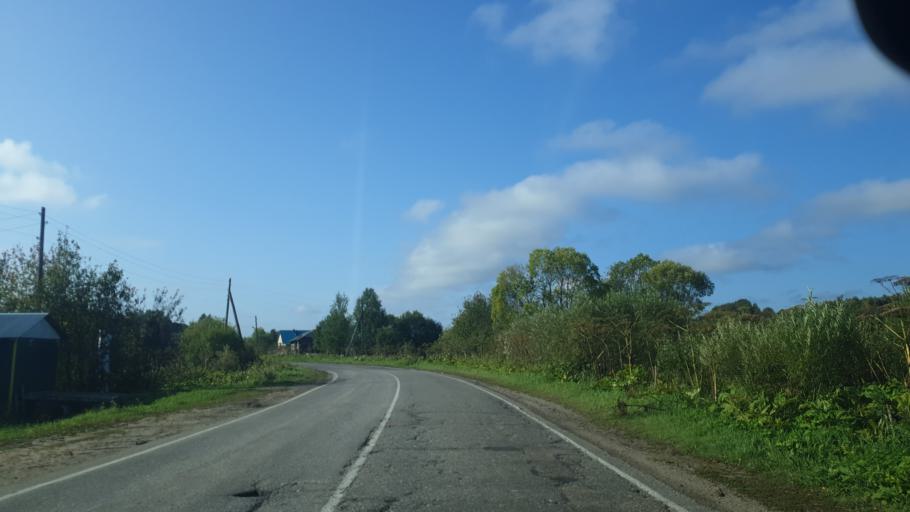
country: RU
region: Komi Republic
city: Vizinga
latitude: 60.9360
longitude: 50.2293
